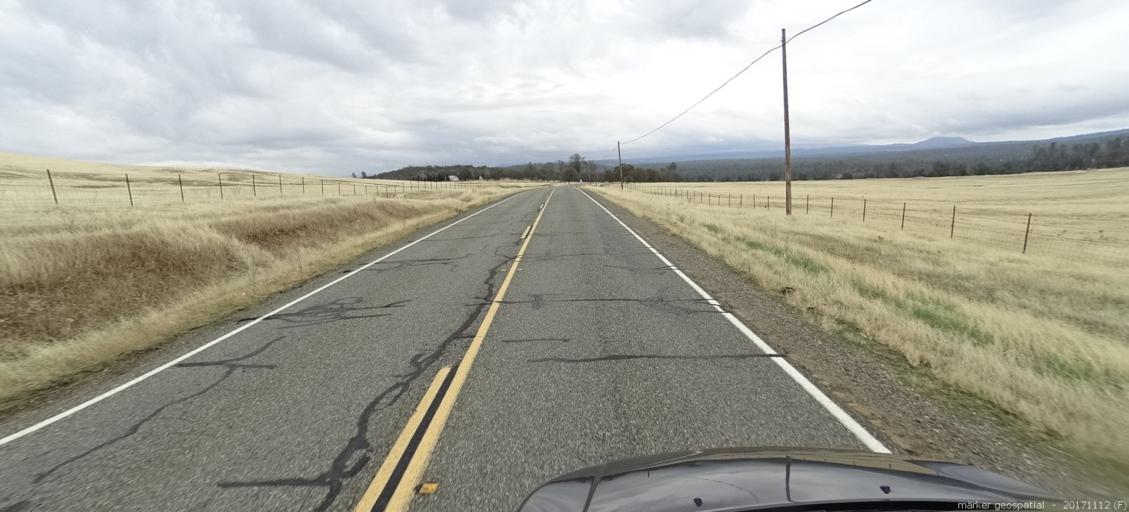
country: US
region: California
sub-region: Shasta County
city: Palo Cedro
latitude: 40.4829
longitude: -122.1635
